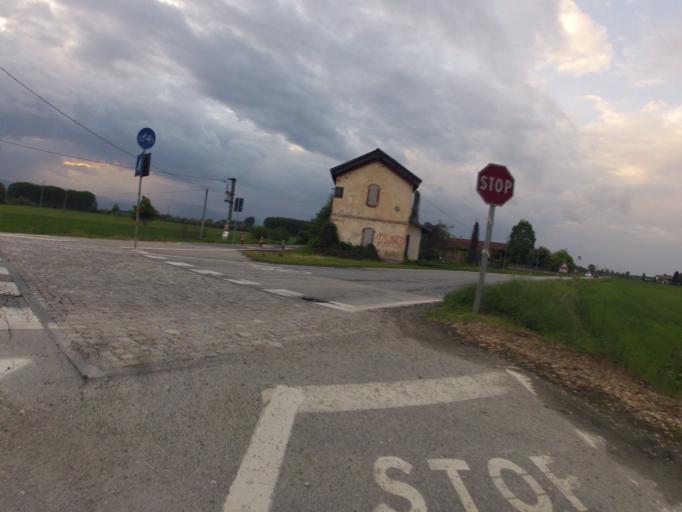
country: IT
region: Piedmont
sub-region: Provincia di Torino
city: Vigone
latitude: 44.8163
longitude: 7.4981
